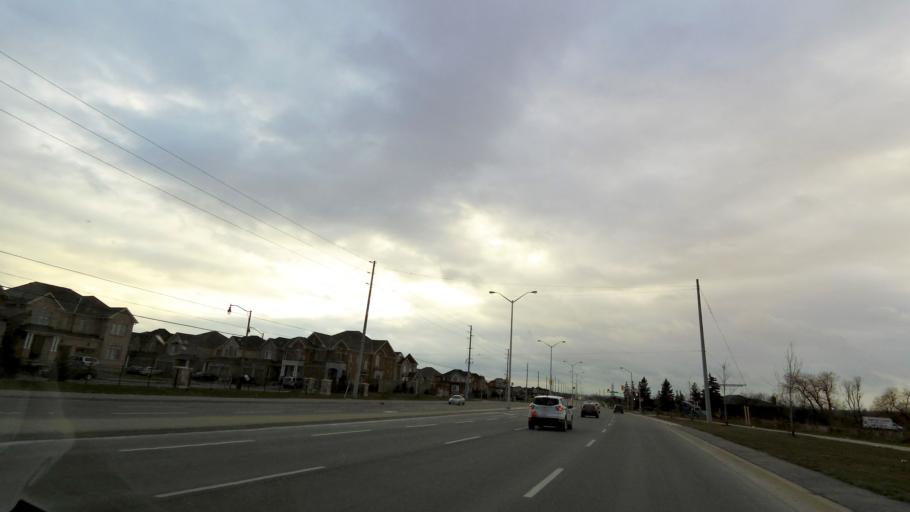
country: CA
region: Ontario
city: Brampton
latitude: 43.8002
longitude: -79.6803
